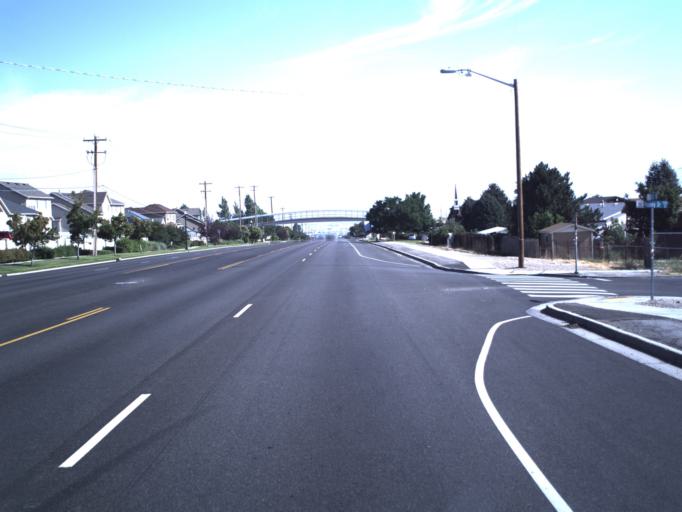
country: US
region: Utah
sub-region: Salt Lake County
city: Oquirrh
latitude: 40.6565
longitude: -112.0246
